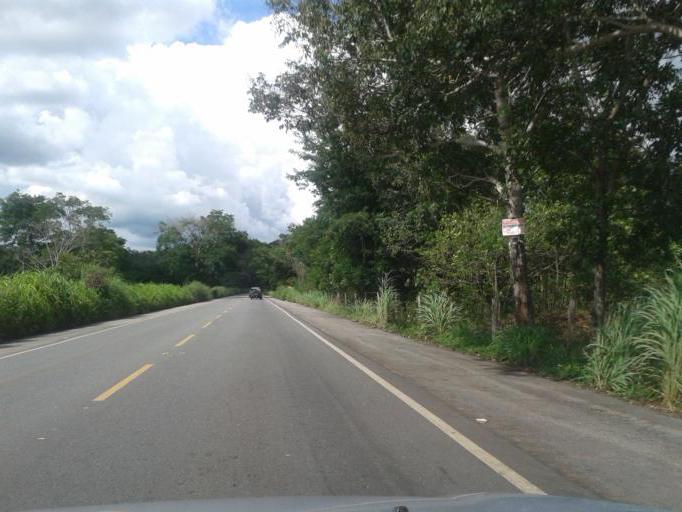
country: BR
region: Goias
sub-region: Goias
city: Goias
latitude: -15.8826
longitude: -50.1045
